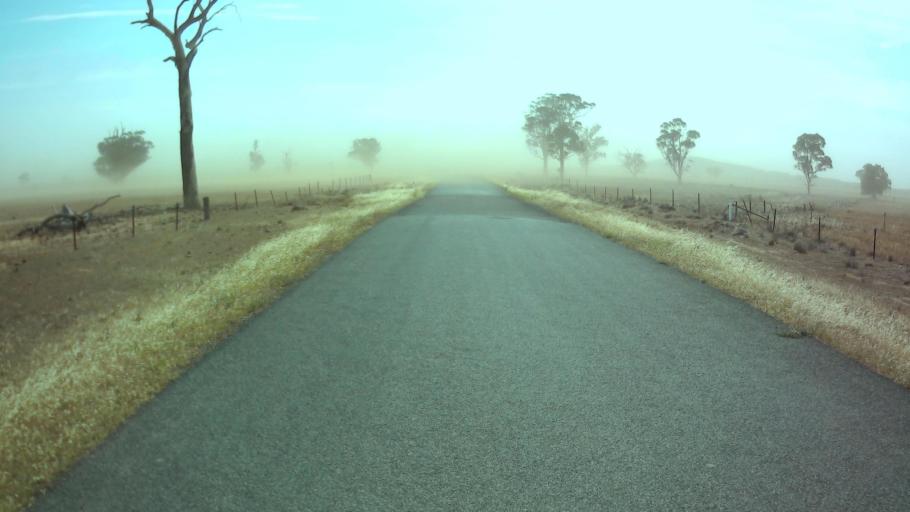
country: AU
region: New South Wales
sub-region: Weddin
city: Grenfell
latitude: -33.7368
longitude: 147.9948
